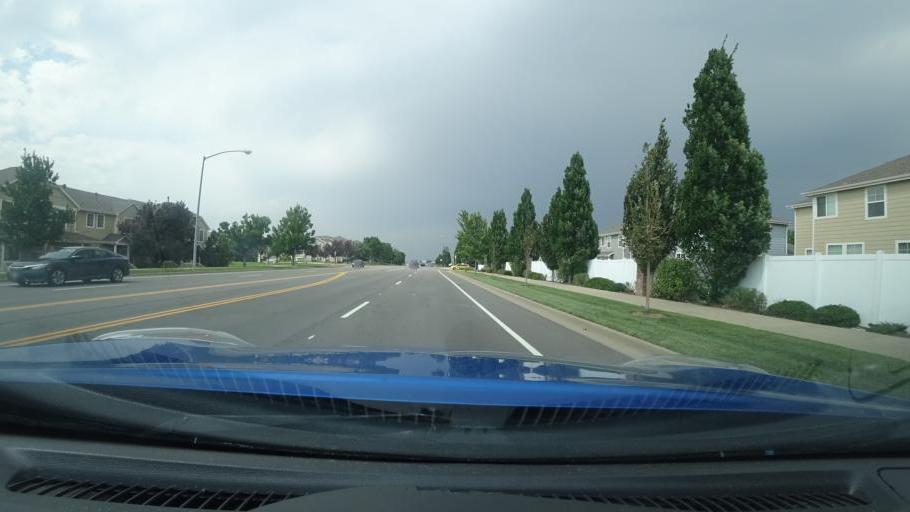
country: US
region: Colorado
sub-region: Adams County
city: Aurora
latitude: 39.6901
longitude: -104.7630
